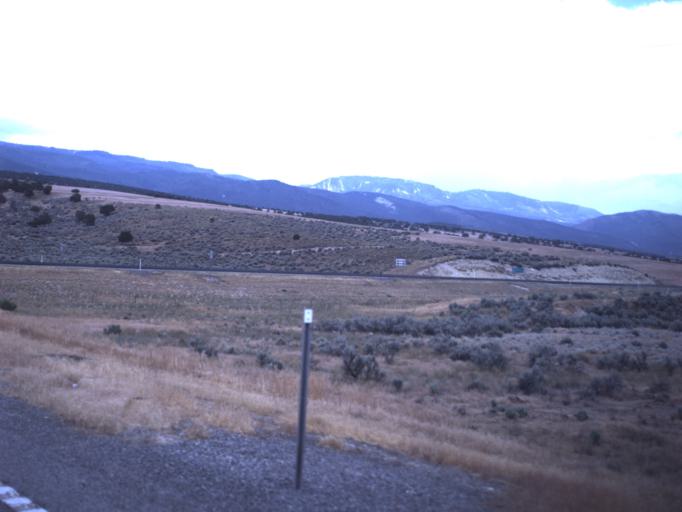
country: US
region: Utah
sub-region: Sanpete County
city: Ephraim
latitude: 39.4221
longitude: -111.5601
